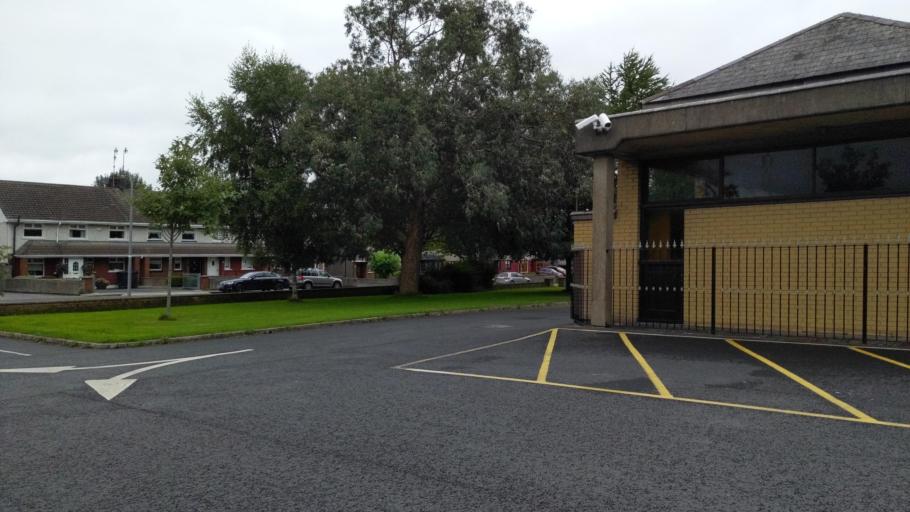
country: IE
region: Leinster
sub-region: Lu
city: Drogheda
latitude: 53.7121
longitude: -6.3598
